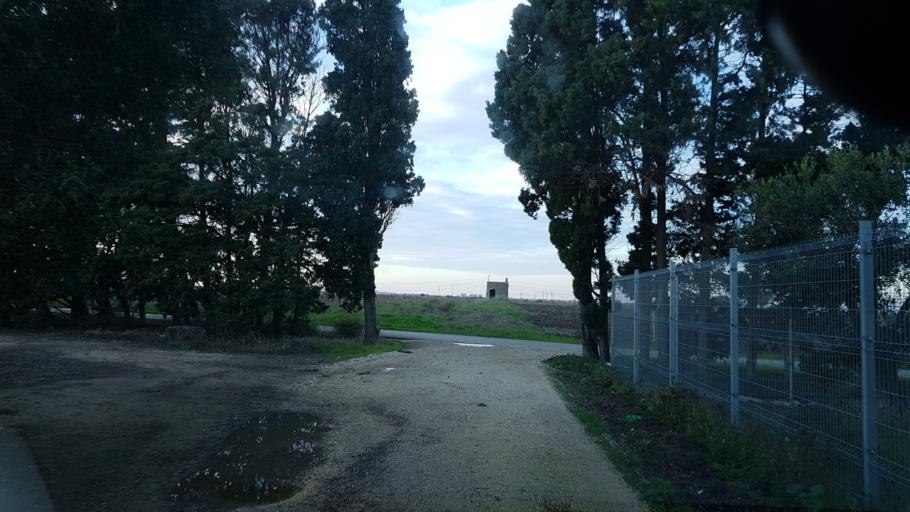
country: IT
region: Apulia
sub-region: Provincia di Brindisi
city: La Rosa
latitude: 40.5945
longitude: 17.9838
